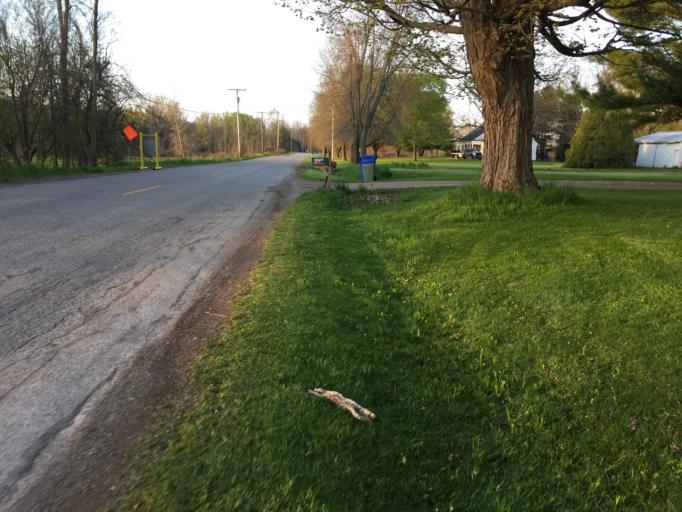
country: US
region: New York
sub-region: Wayne County
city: Marion
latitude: 43.1463
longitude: -77.1699
